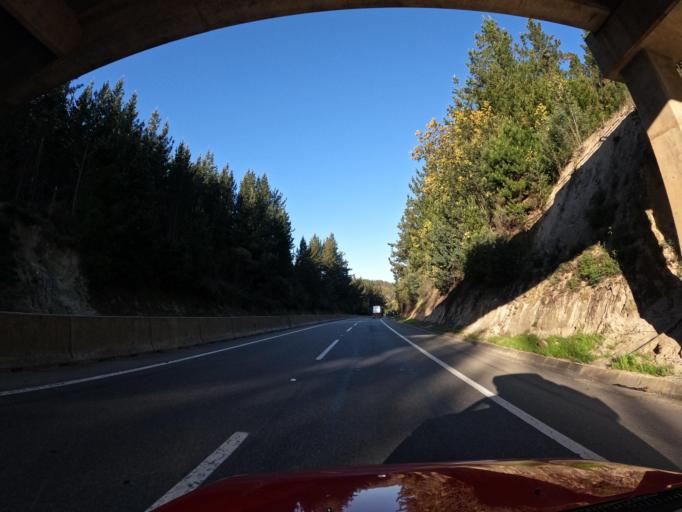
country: CL
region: Biobio
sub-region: Provincia de Concepcion
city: Tome
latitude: -36.7323
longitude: -72.8024
